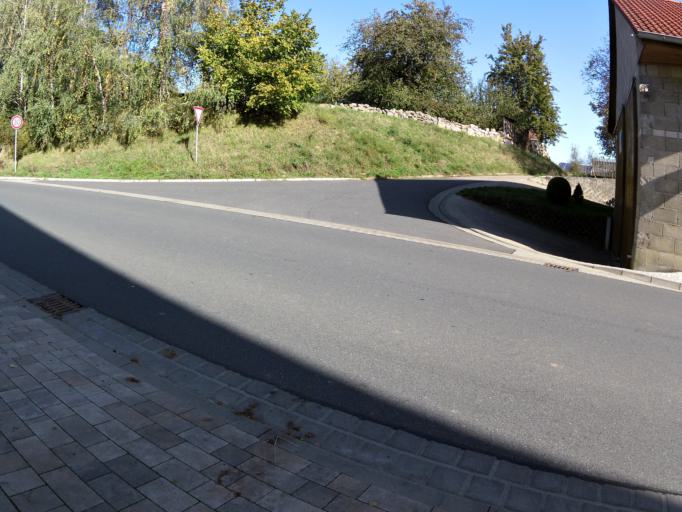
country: DE
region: Bavaria
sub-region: Regierungsbezirk Unterfranken
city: Biebelried
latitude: 49.7649
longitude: 10.0787
